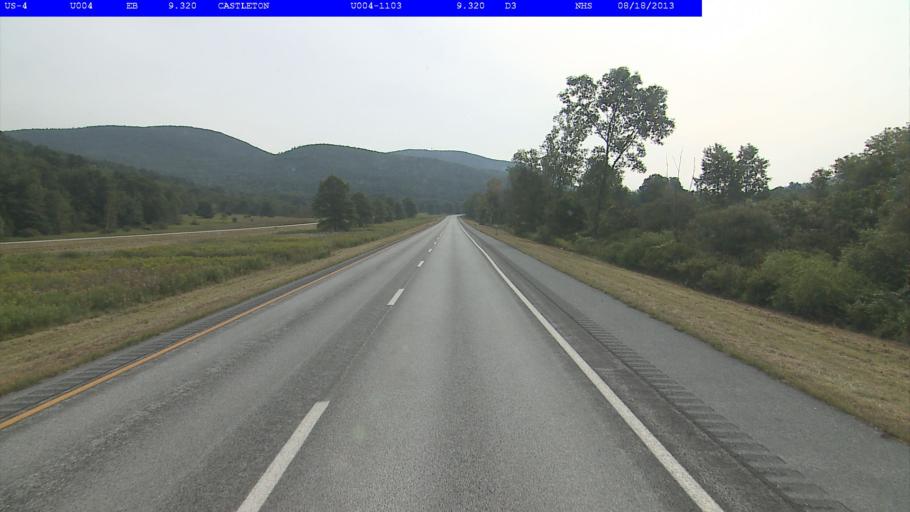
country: US
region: Vermont
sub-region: Rutland County
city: Castleton
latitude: 43.6158
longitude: -73.1359
